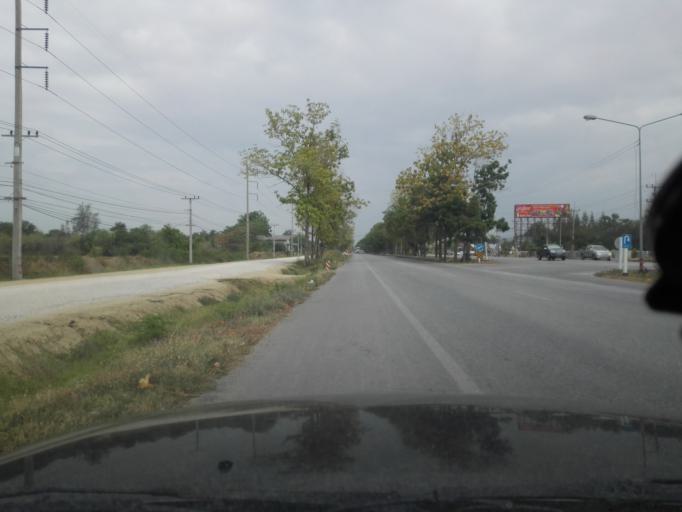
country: TH
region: Nakhon Sawan
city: Nakhon Sawan
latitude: 15.7229
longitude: 100.0484
